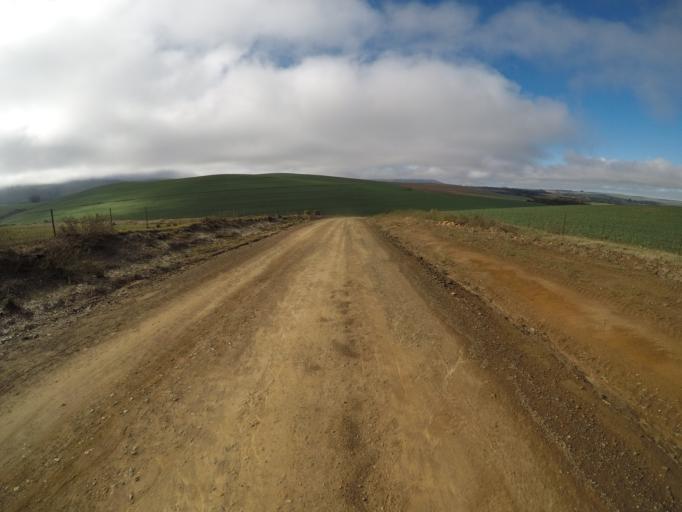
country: ZA
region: Western Cape
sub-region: Overberg District Municipality
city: Caledon
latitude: -34.1095
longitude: 19.7654
